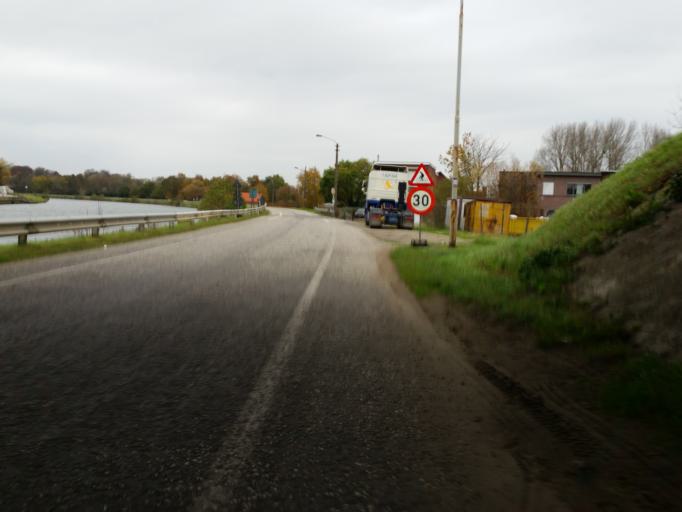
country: BE
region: Flanders
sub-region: Provincie Antwerpen
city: Lier
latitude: 51.1278
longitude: 4.5927
